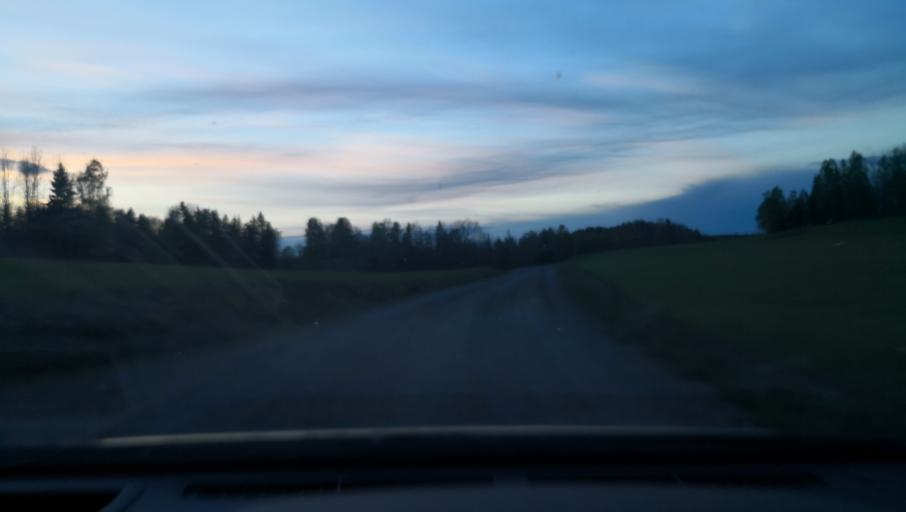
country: SE
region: OErebro
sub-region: Askersunds Kommun
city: Askersund
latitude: 58.9910
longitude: 14.9070
